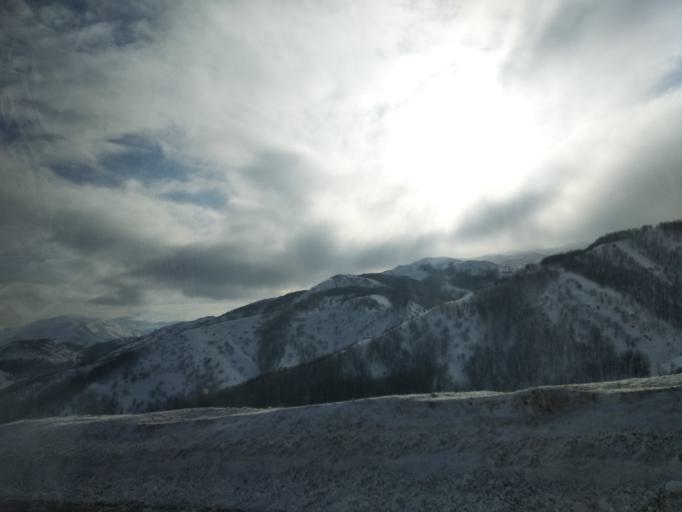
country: TR
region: Erzincan
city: Catalarmut
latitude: 39.8958
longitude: 39.3886
